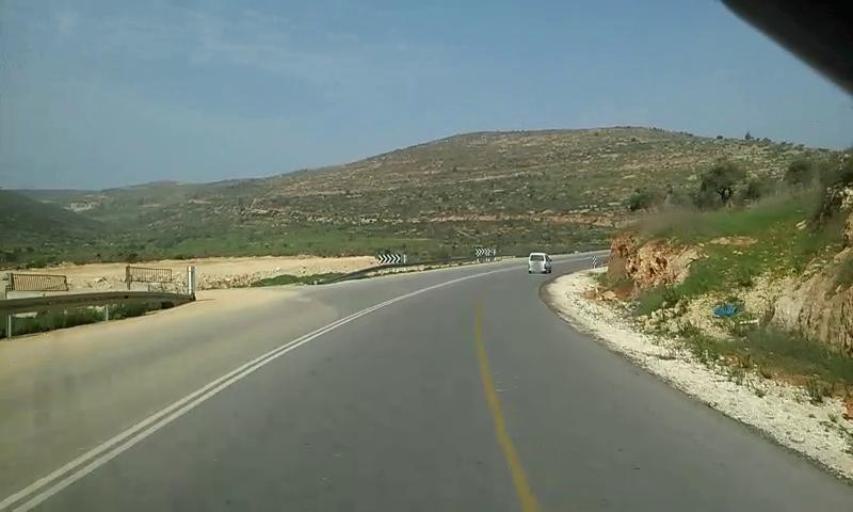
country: PS
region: West Bank
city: `Atarah
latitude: 31.9866
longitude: 35.2280
